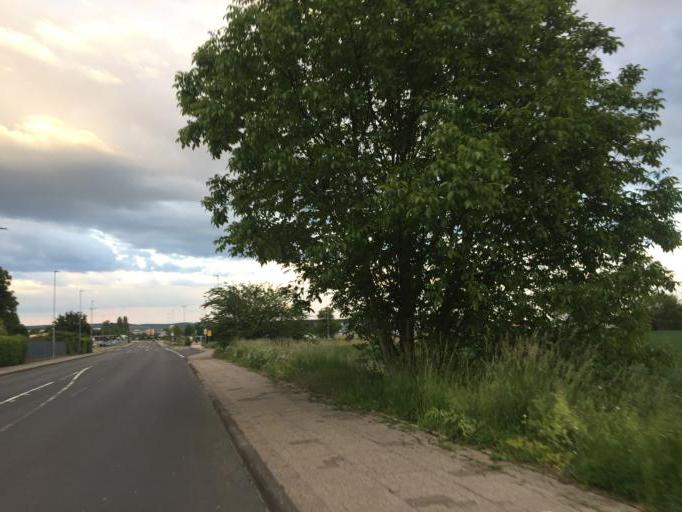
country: DE
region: Hesse
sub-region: Regierungsbezirk Darmstadt
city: Butzbach
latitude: 50.4307
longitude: 8.6788
